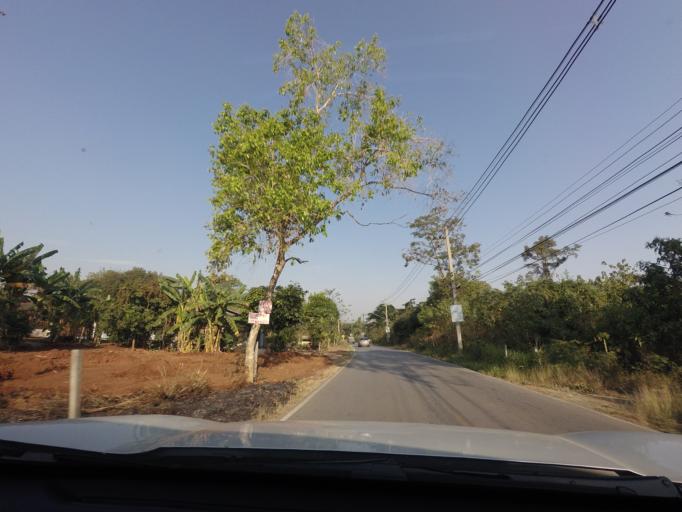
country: TH
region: Nakhon Ratchasima
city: Pak Chong
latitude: 14.6356
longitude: 101.4307
